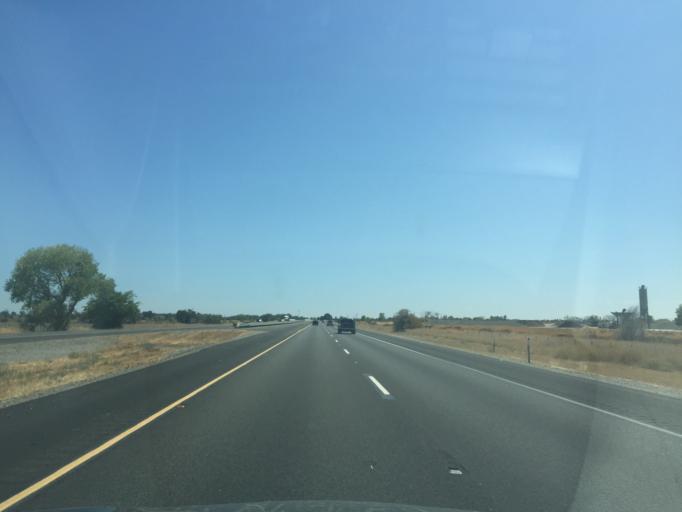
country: US
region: California
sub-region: Tehama County
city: Corning
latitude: 39.9815
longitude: -122.2029
